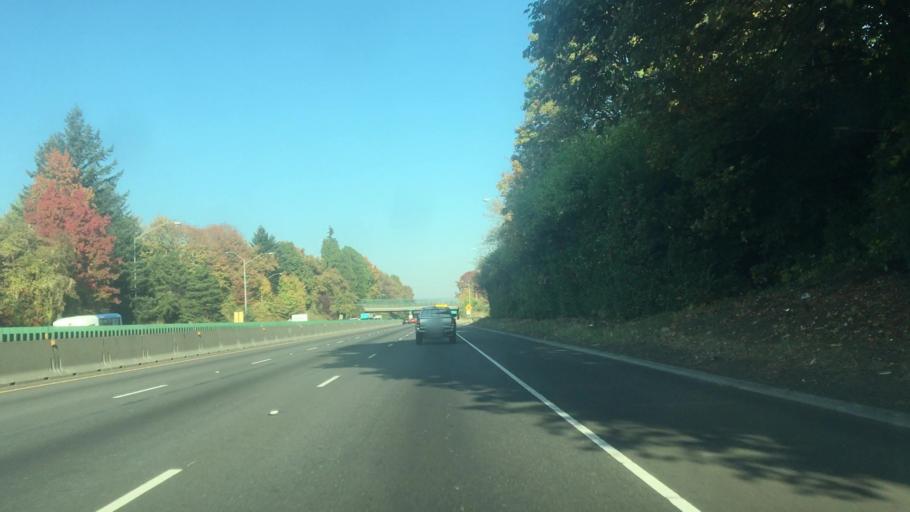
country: US
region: Oregon
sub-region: Clackamas County
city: Lake Oswego
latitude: 45.4615
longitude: -122.7026
